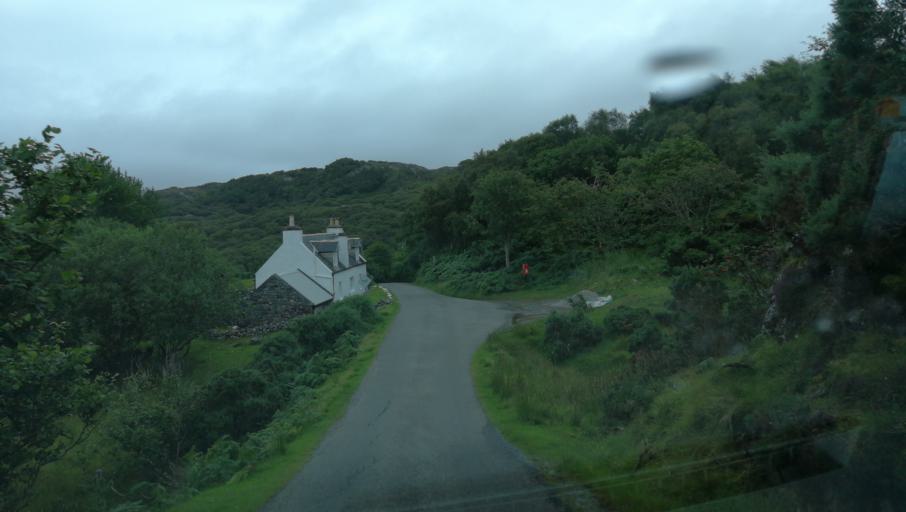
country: GB
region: Scotland
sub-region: Highland
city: Ullapool
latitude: 58.1366
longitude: -5.2611
